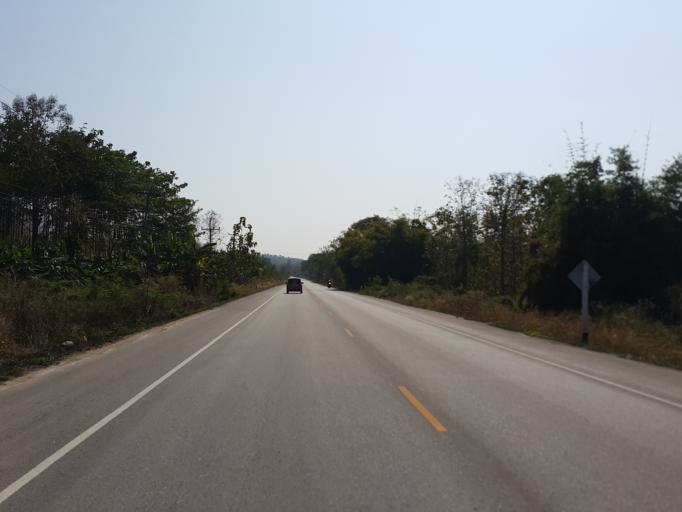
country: TH
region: Lampang
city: Chae Hom
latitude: 18.7935
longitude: 99.5867
